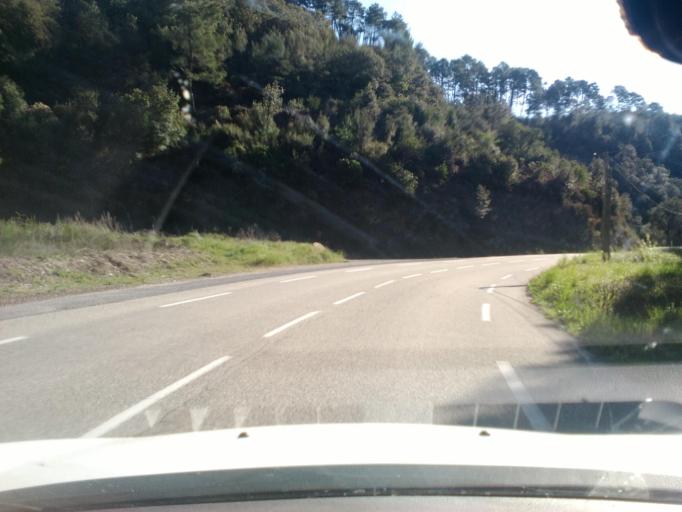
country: FR
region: Languedoc-Roussillon
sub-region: Departement du Gard
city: Saint-Jean-du-Gard
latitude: 44.1100
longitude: 3.8115
